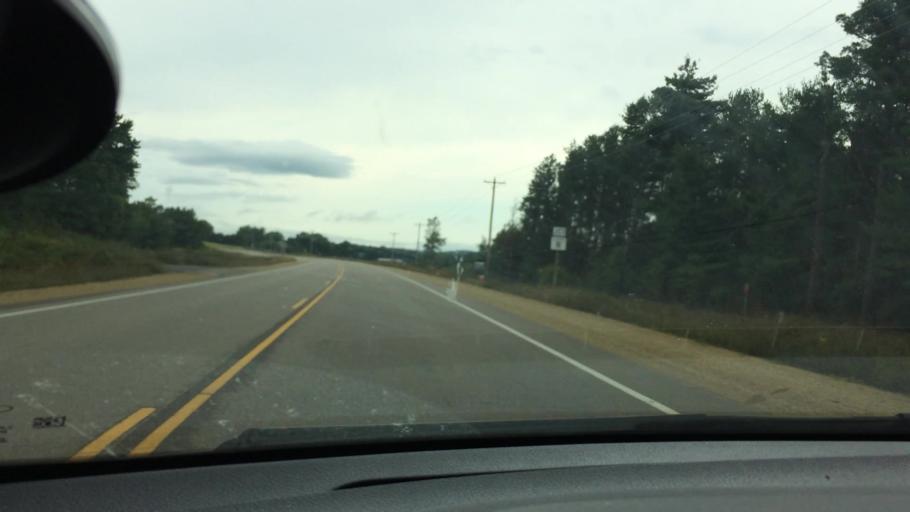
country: US
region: Wisconsin
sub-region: Trempealeau County
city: Osseo
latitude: 44.5902
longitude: -91.1725
